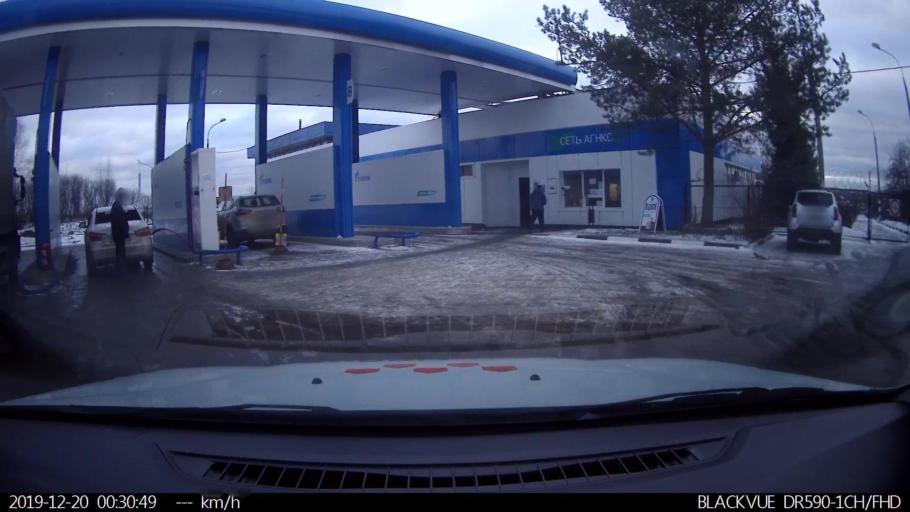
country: RU
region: Vladimir
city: Yur'yev-Pol'skiy
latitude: 56.5171
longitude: 39.6490
